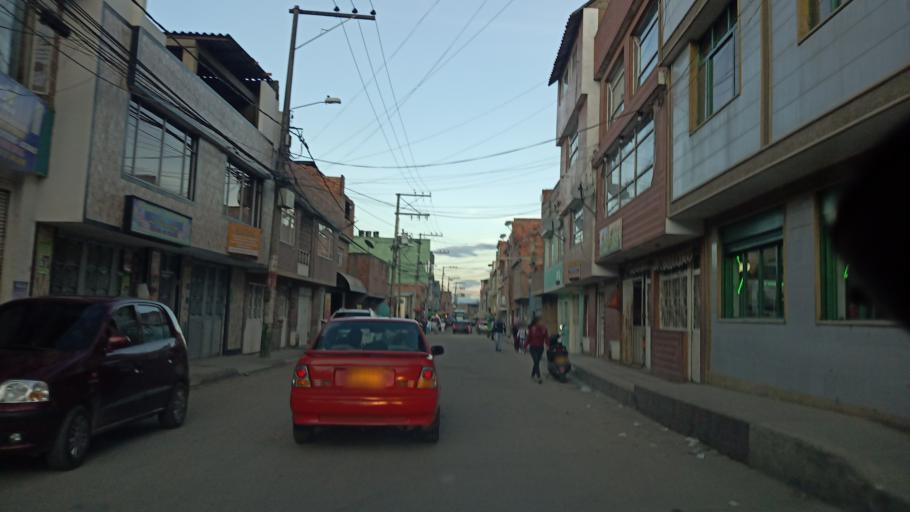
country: CO
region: Cundinamarca
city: Soacha
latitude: 4.5780
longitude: -74.2169
